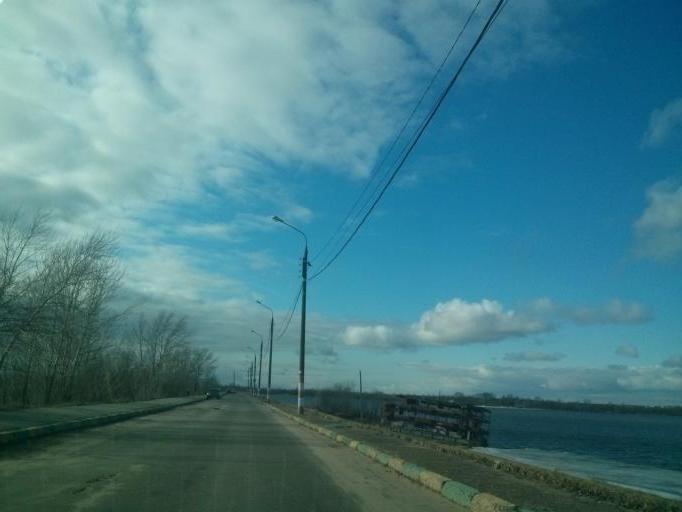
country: RU
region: Nizjnij Novgorod
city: Nizhniy Novgorod
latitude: 56.3310
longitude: 44.0420
